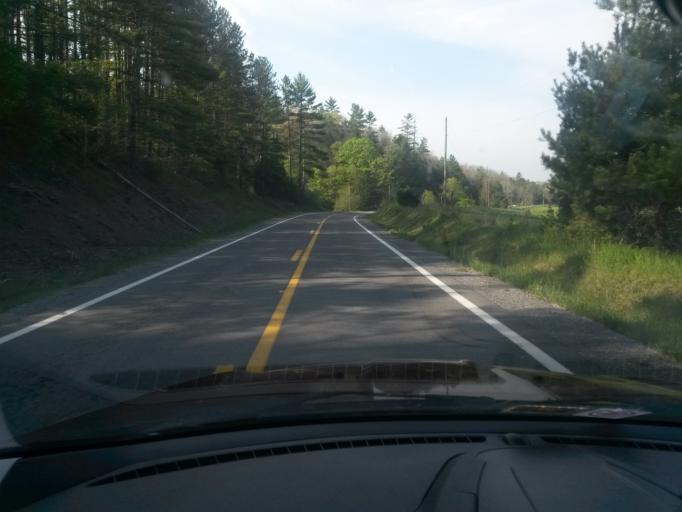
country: US
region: West Virginia
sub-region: Pocahontas County
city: Marlinton
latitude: 38.1167
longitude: -79.9553
